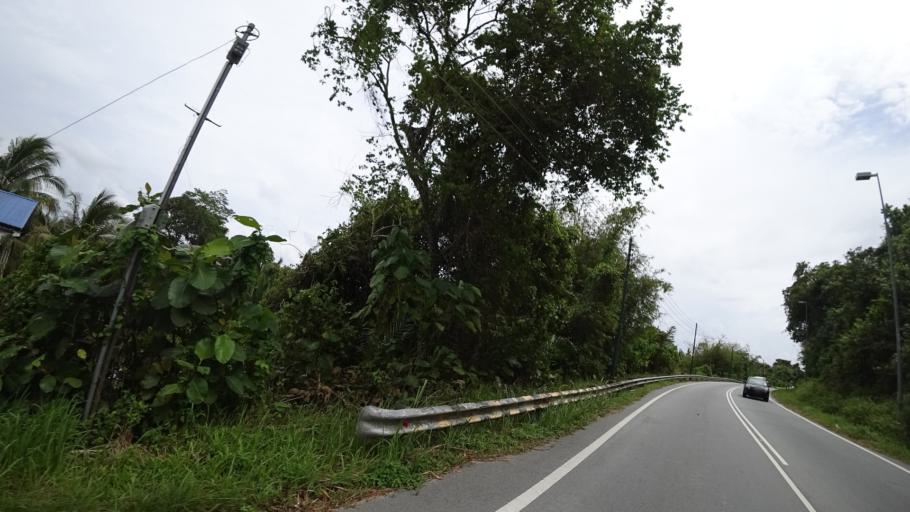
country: BN
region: Tutong
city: Tutong
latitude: 4.8052
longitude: 114.6721
